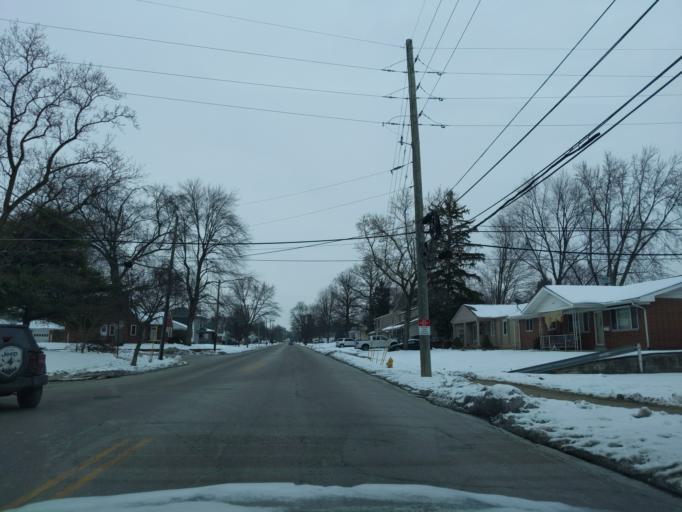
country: US
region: Indiana
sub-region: Tippecanoe County
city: Lafayette
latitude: 40.4025
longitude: -86.8767
